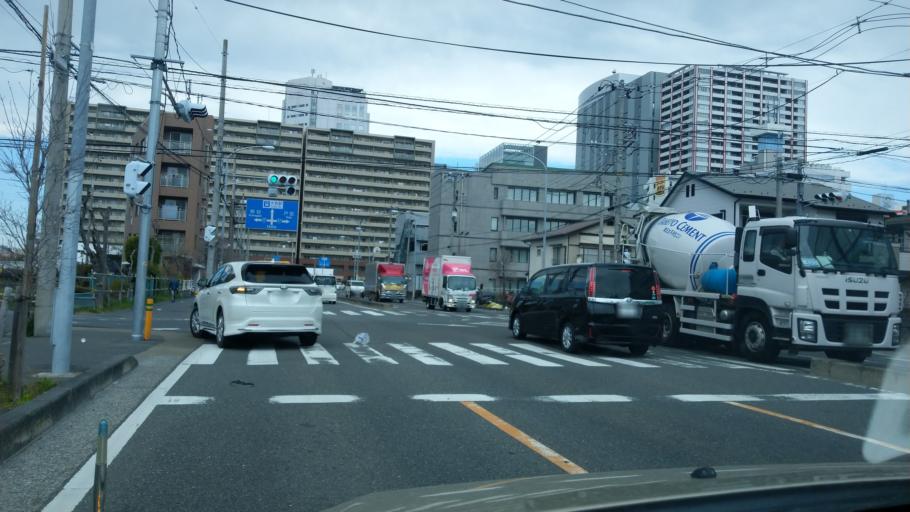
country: JP
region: Saitama
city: Yono
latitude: 35.9008
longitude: 139.6191
